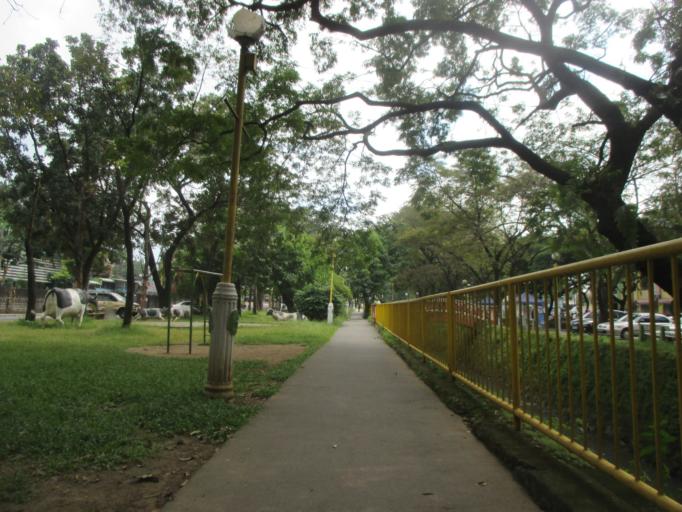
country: PH
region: Calabarzon
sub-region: Province of Rizal
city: Antipolo
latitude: 14.6511
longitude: 121.1156
